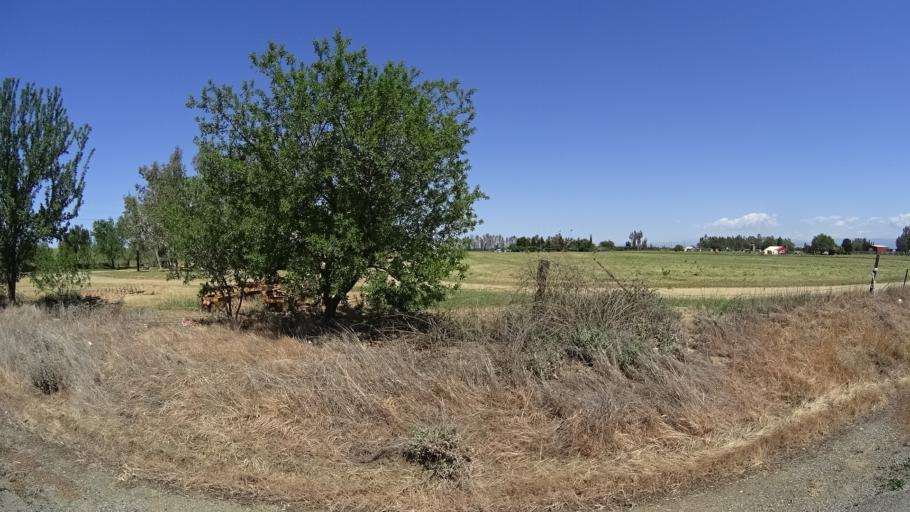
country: US
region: California
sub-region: Glenn County
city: Orland
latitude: 39.7977
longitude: -122.1546
